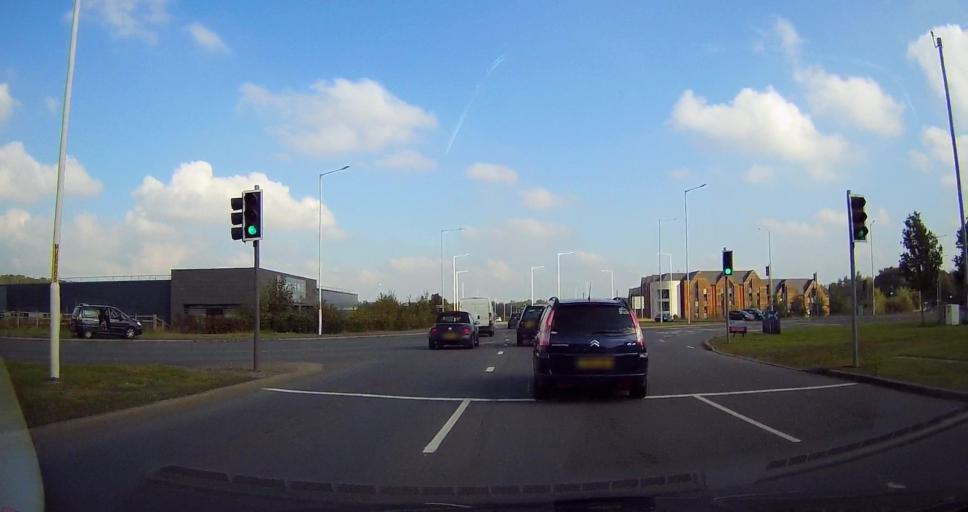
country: GB
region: England
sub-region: Kent
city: Ashford
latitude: 51.1573
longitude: 0.8602
